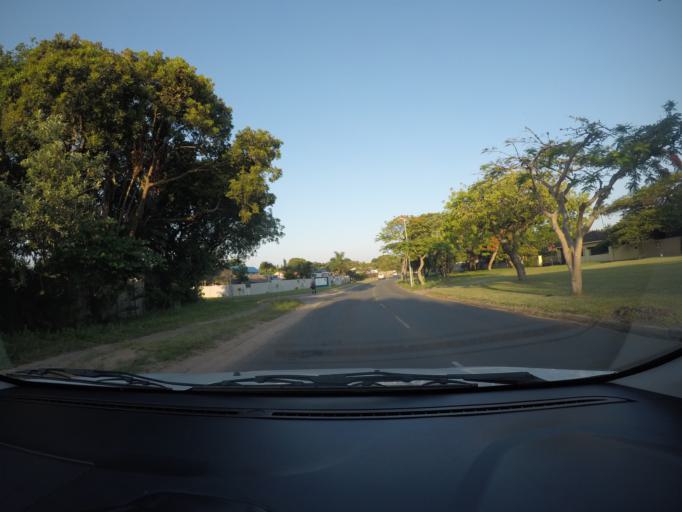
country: ZA
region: KwaZulu-Natal
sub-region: uThungulu District Municipality
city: Richards Bay
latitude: -28.7772
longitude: 32.1019
